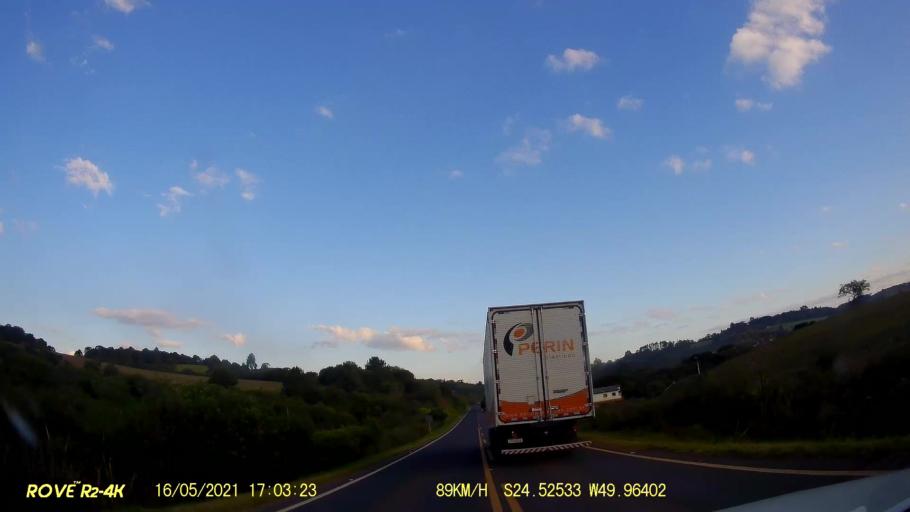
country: BR
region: Parana
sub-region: Pirai Do Sul
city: Pirai do Sul
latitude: -24.5251
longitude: -49.9639
